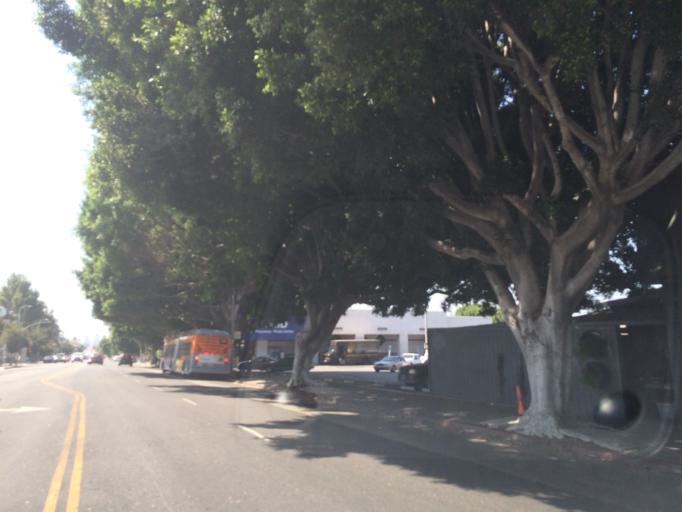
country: US
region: California
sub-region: Los Angeles County
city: Hollywood
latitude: 34.1053
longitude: -118.3093
